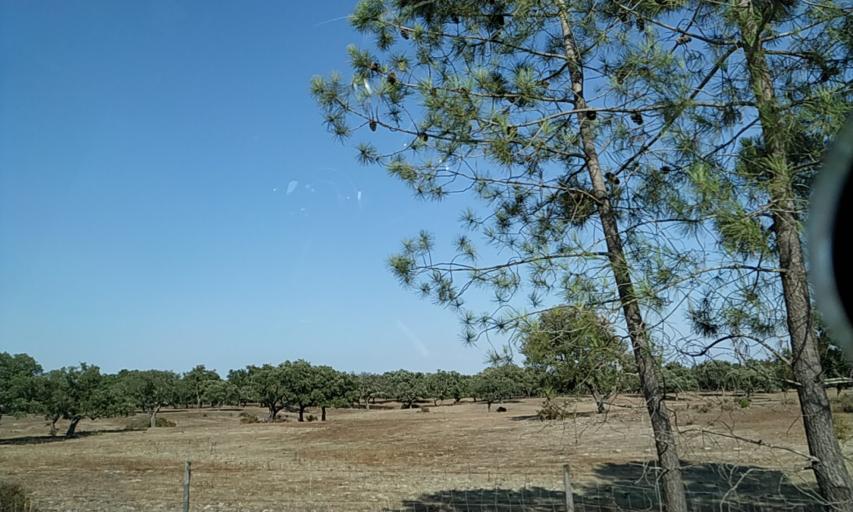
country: PT
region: Santarem
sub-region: Coruche
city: Coruche
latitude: 38.9145
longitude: -8.5253
